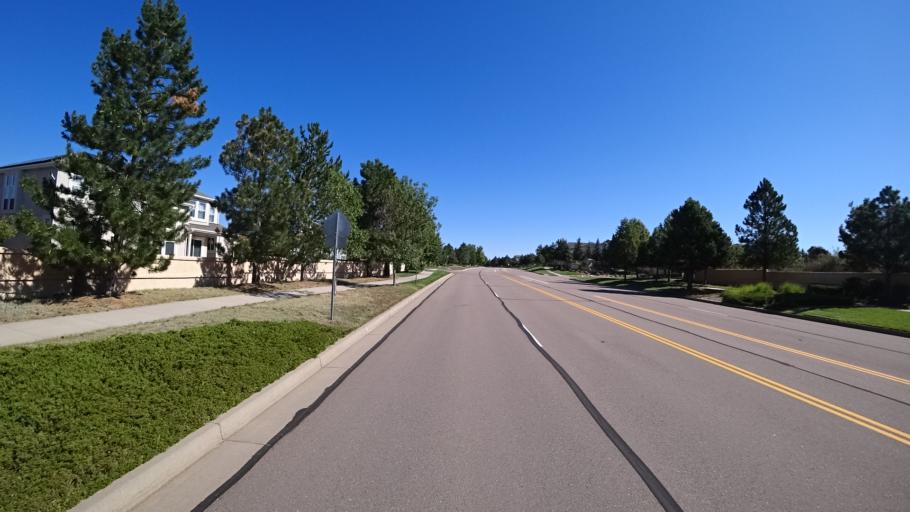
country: US
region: Colorado
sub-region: El Paso County
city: Black Forest
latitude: 38.9777
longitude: -104.7707
